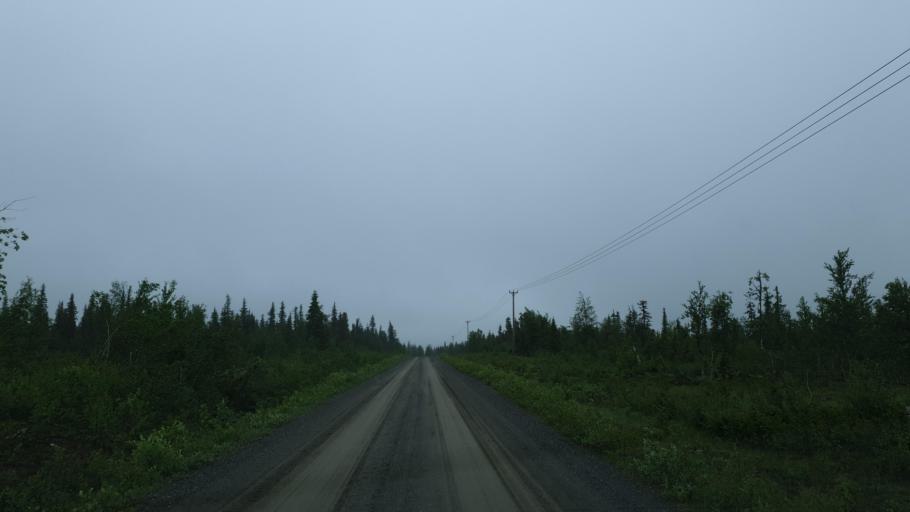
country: SE
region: Vaesterbotten
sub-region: Vilhelmina Kommun
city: Sjoberg
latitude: 65.3135
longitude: 15.9626
